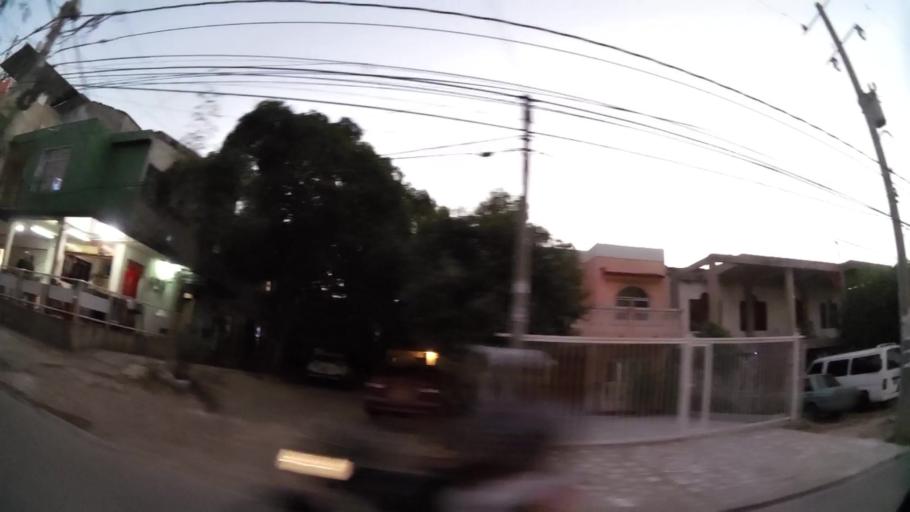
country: CO
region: Bolivar
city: Cartagena
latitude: 10.3865
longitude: -75.4940
